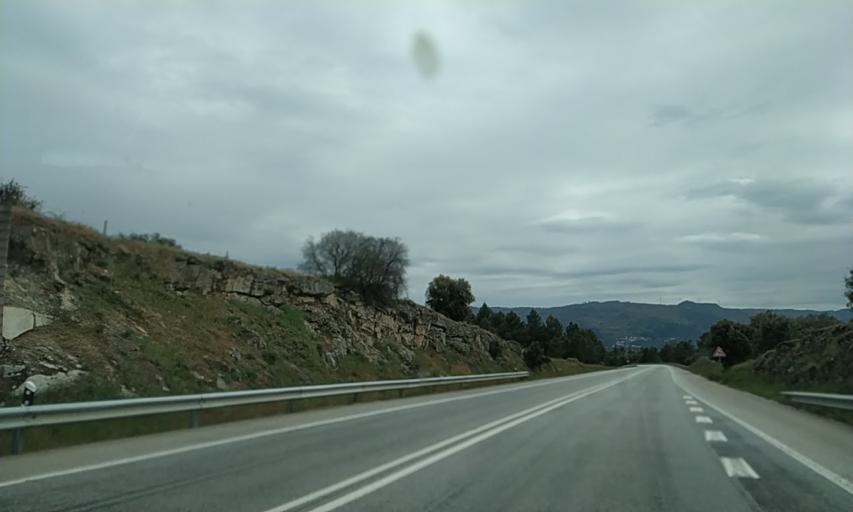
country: PT
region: Guarda
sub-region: Celorico da Beira
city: Celorico da Beira
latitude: 40.6279
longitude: -7.3079
